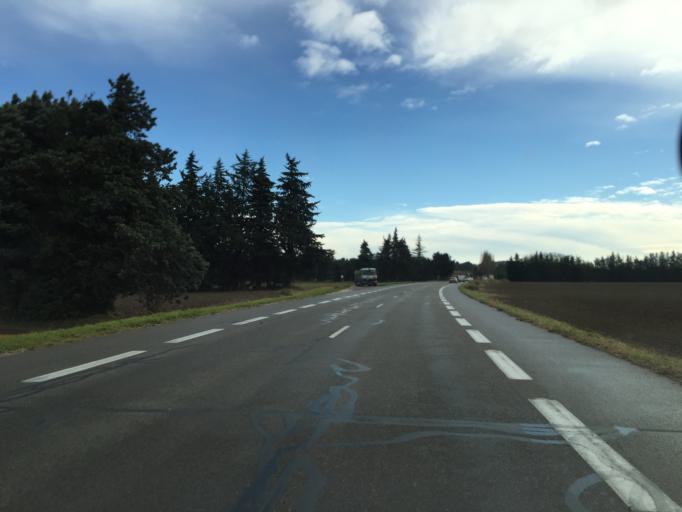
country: FR
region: Provence-Alpes-Cote d'Azur
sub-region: Departement du Vaucluse
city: Velleron
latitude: 43.9660
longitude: 5.0239
